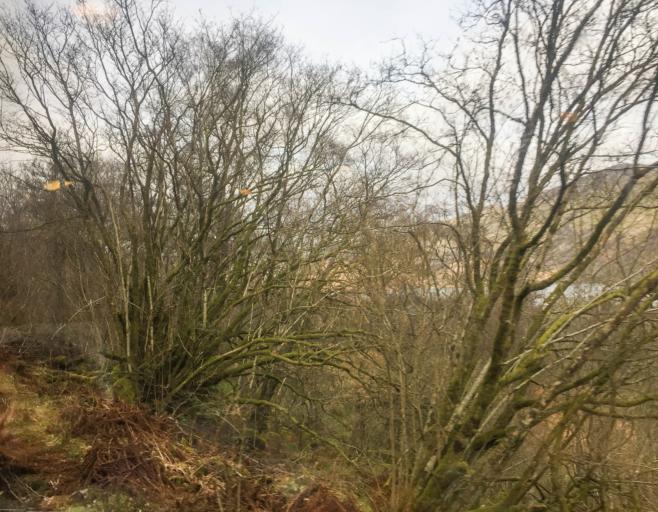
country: GB
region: Scotland
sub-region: Argyll and Bute
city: Garelochhead
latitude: 56.2859
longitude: -4.7096
